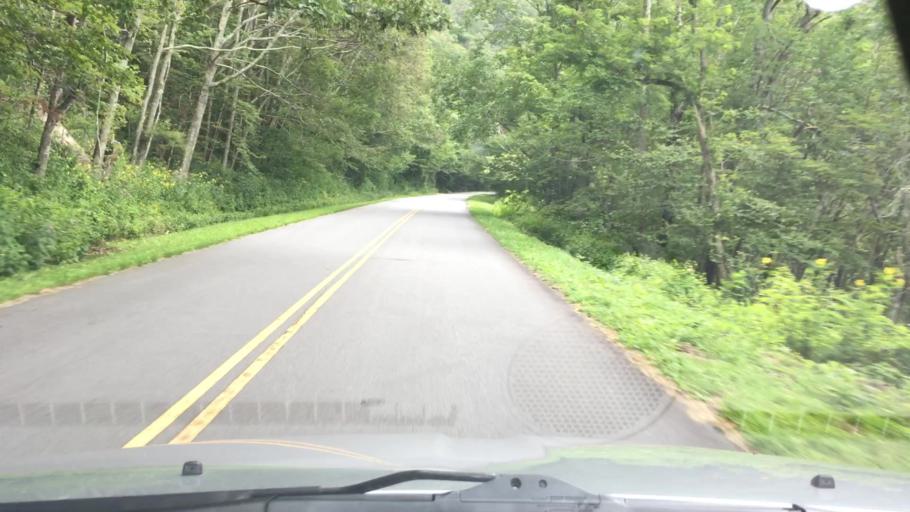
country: US
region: North Carolina
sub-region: Buncombe County
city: Swannanoa
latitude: 35.6968
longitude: -82.3939
